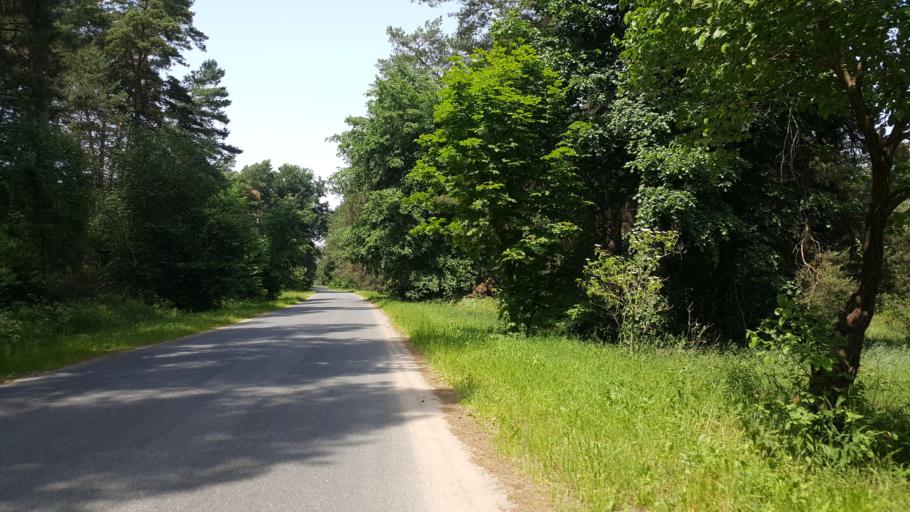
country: BY
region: Brest
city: Kamyanyuki
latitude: 52.5012
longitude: 23.8647
